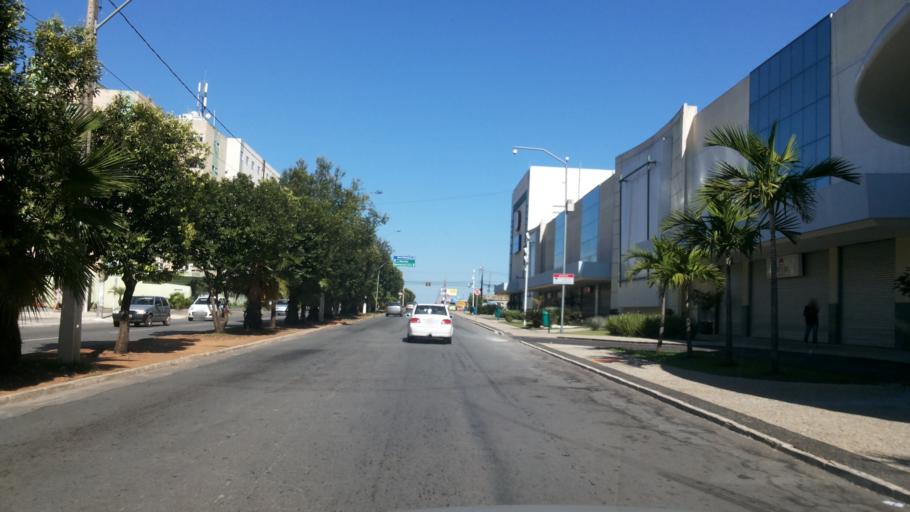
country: BR
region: Goias
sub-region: Goiania
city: Goiania
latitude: -16.7420
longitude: -49.2767
